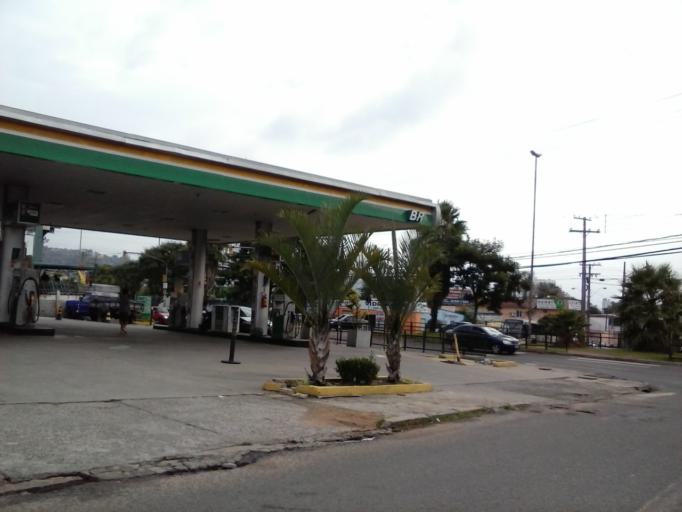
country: BR
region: Rio Grande do Sul
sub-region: Porto Alegre
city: Porto Alegre
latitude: -30.0554
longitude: -51.1472
